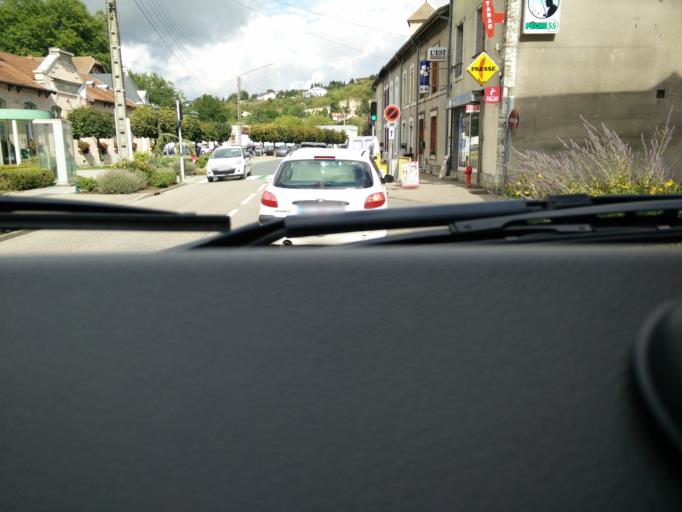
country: FR
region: Lorraine
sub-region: Departement de la Meuse
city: Verdun
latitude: 49.1744
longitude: 5.3810
